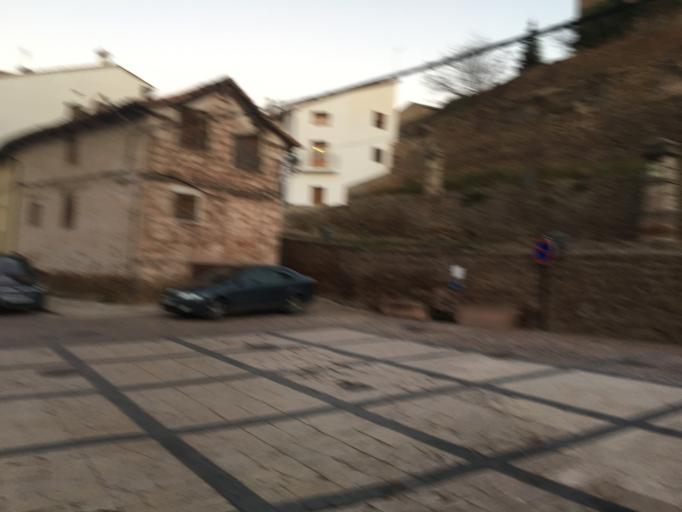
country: ES
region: Aragon
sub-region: Provincia de Teruel
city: Mora de Rubielos
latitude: 40.2523
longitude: -0.7518
